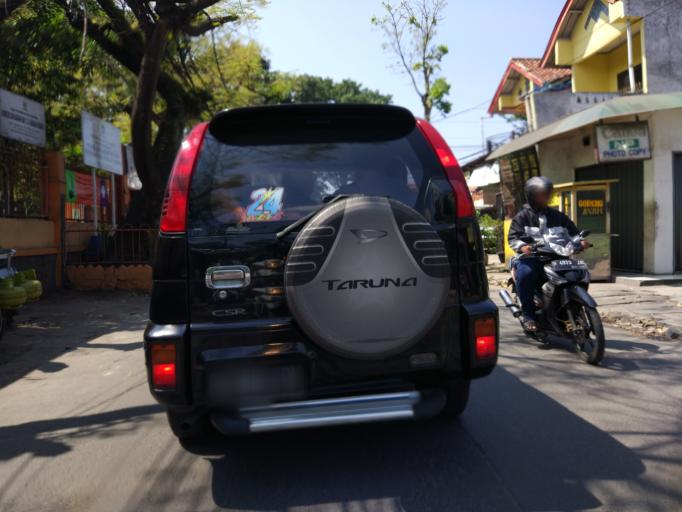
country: ID
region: West Java
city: Bandung
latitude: -6.9244
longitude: 107.6540
